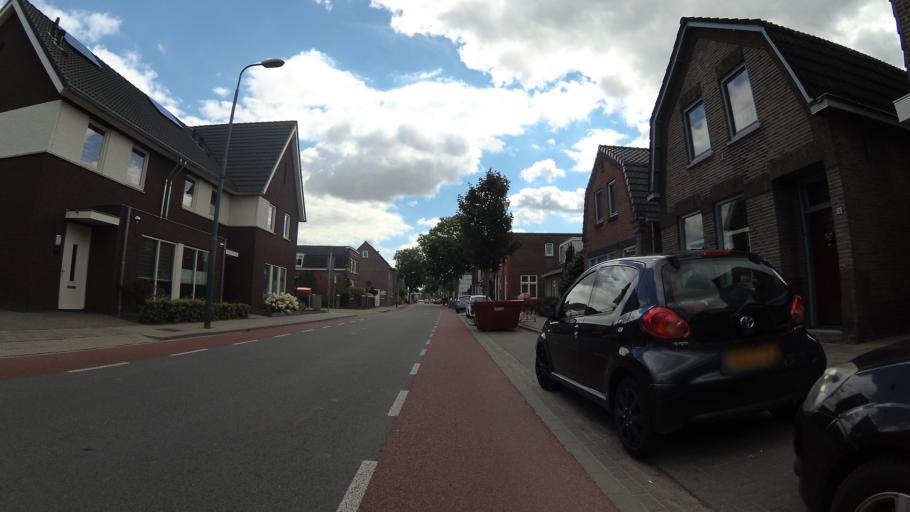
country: NL
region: North Brabant
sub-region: Gemeente Waalwijk
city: Waalwijk
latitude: 51.6578
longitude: 5.0385
